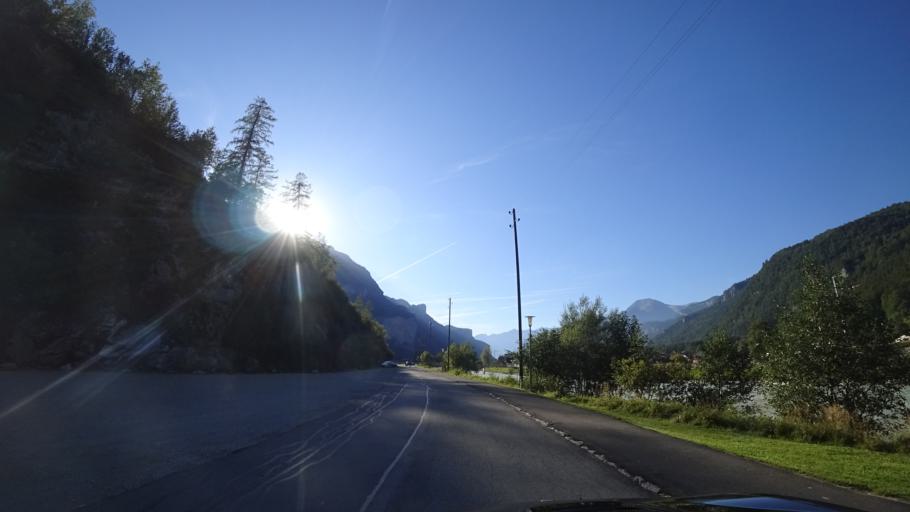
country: CH
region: Bern
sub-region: Interlaken-Oberhasli District
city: Meiringen
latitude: 46.7206
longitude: 8.2009
